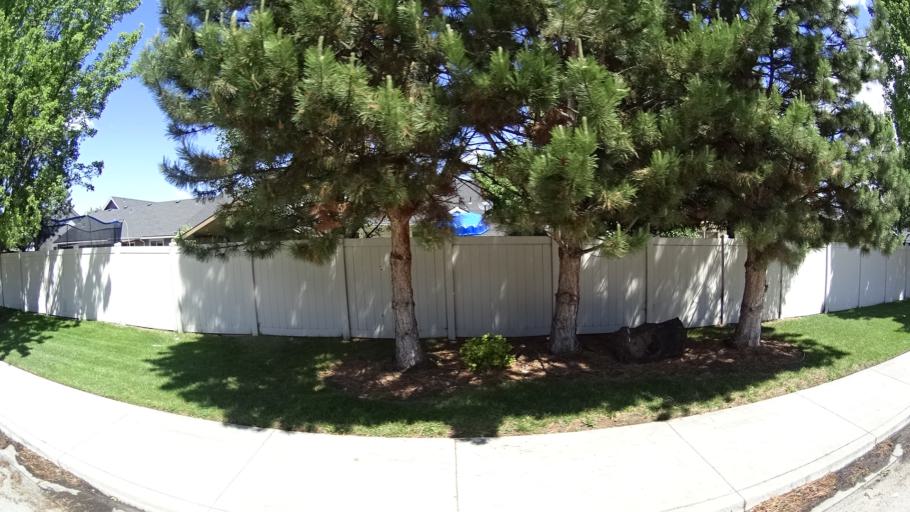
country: US
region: Idaho
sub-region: Ada County
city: Meridian
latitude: 43.6286
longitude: -116.3353
